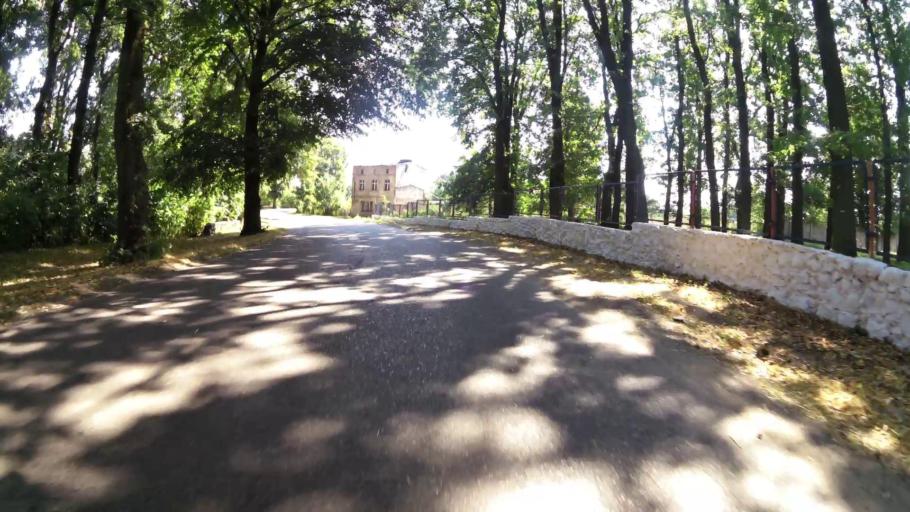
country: PL
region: West Pomeranian Voivodeship
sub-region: Powiat walecki
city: Walcz
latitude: 53.2015
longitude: 16.4933
